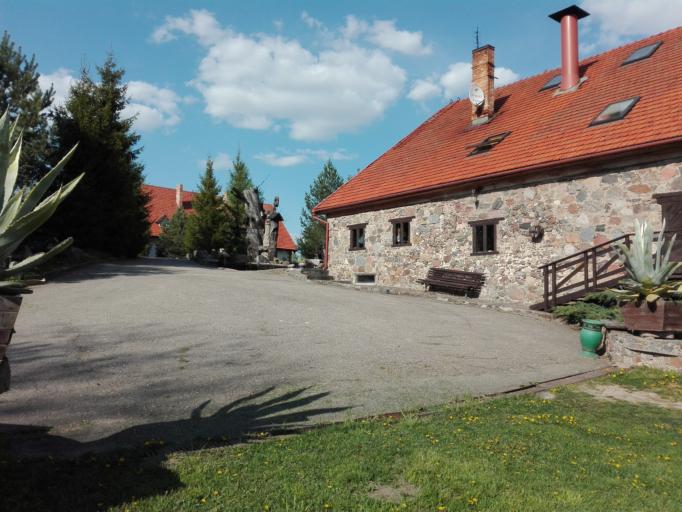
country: LT
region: Panevezys
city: Pasvalys
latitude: 56.0342
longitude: 24.3529
